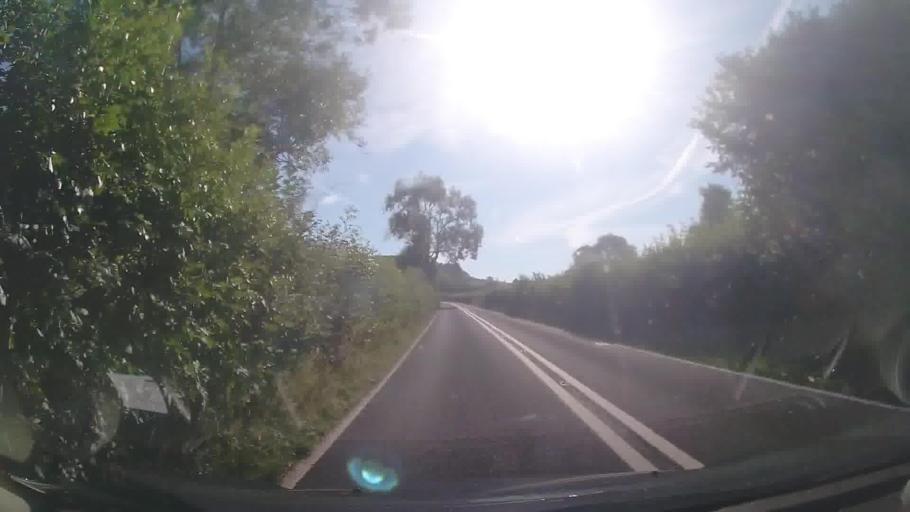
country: GB
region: Wales
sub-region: Sir Powys
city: Hay
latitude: 51.9676
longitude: -3.2137
